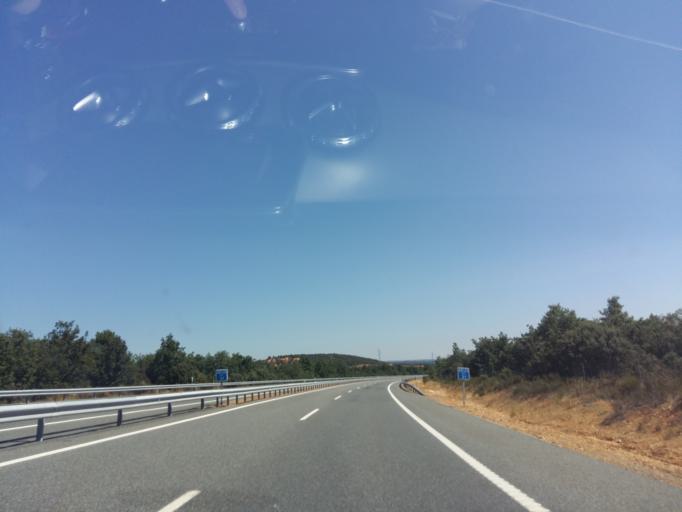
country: ES
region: Castille and Leon
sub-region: Provincia de Leon
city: San Justo de la Vega
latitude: 42.4470
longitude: -5.9733
